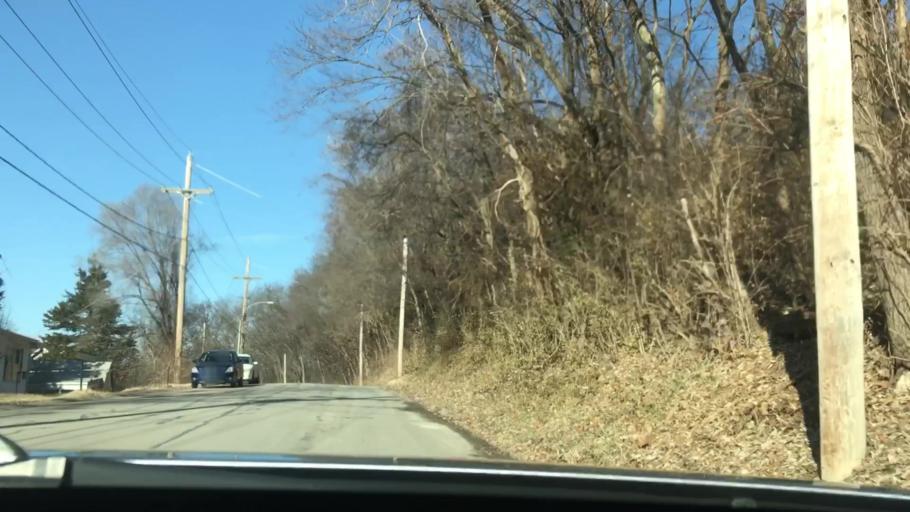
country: US
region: Missouri
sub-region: Platte County
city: Parkville
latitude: 39.1964
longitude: -94.6840
